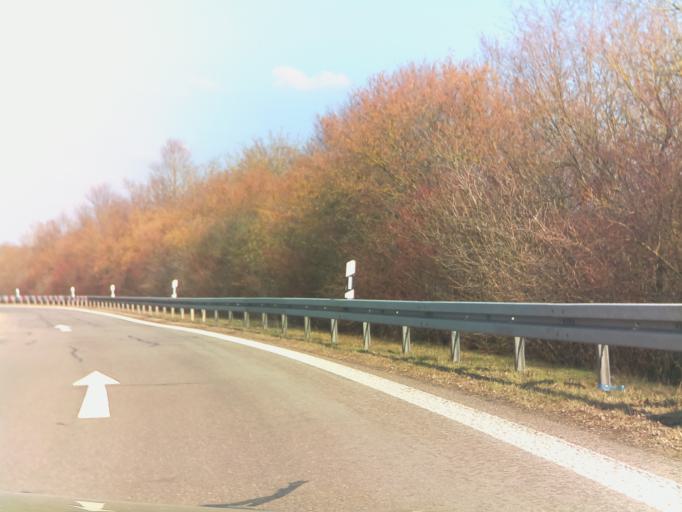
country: DE
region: Baden-Wuerttemberg
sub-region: Karlsruhe Region
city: Empfingen
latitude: 48.4305
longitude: 8.7493
